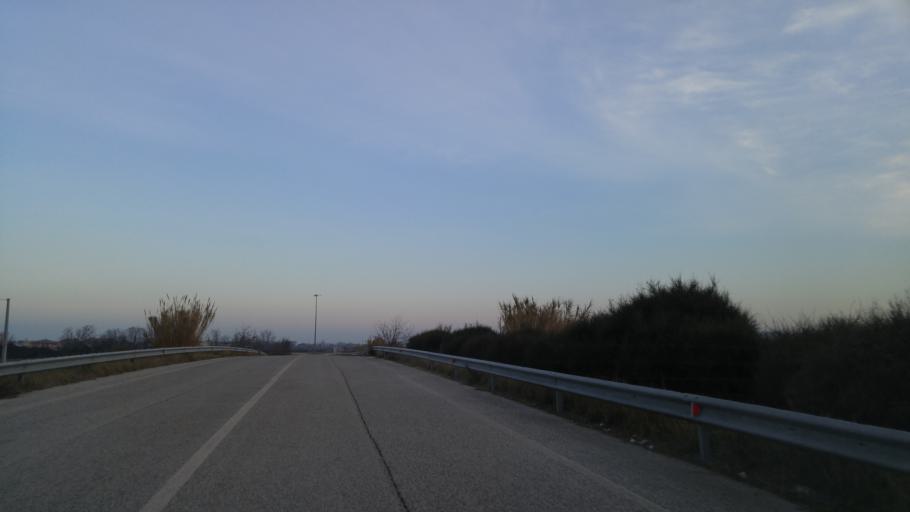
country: IT
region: The Marches
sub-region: Provincia di Pesaro e Urbino
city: Marotta
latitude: 43.7618
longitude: 13.1406
